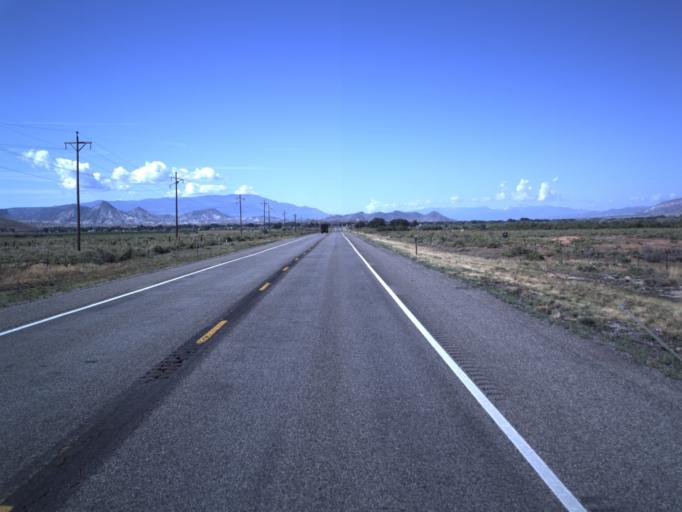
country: US
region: Utah
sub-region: Sevier County
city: Salina
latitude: 38.9982
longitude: -111.8426
